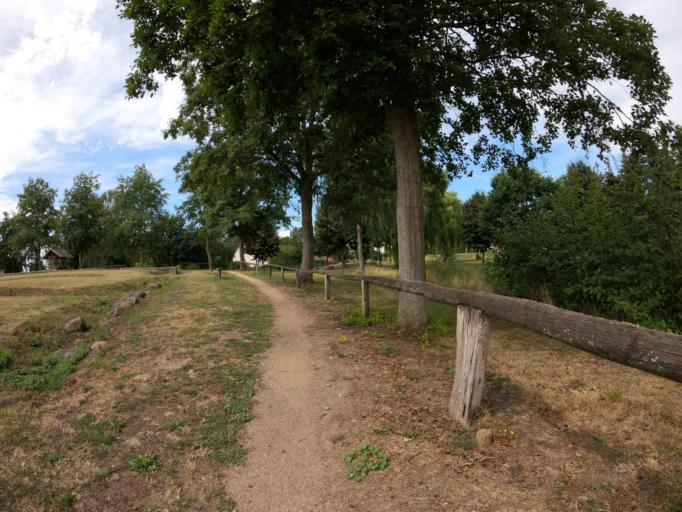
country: DE
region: Mecklenburg-Vorpommern
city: Loitz
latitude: 53.4406
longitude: 13.4635
